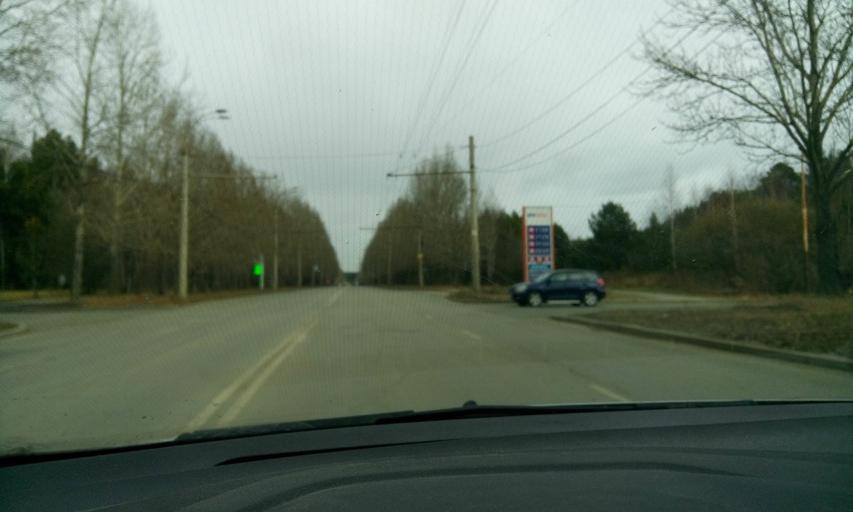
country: RU
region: Sverdlovsk
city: Sovkhoznyy
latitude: 56.7728
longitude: 60.5459
